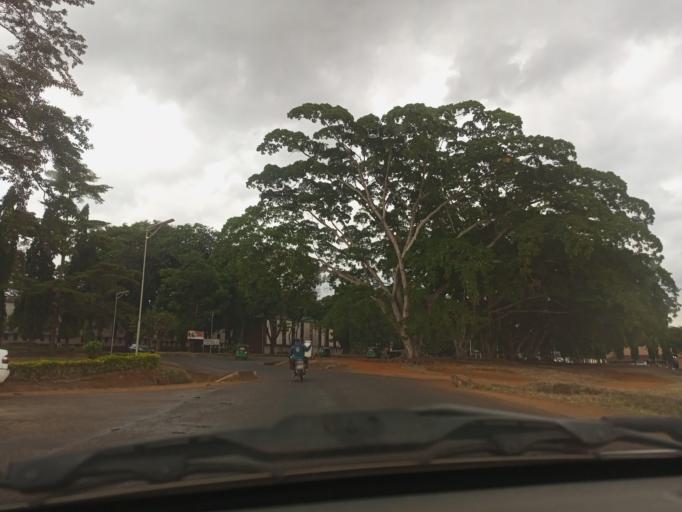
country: TZ
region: Morogoro
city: Morogoro
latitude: -6.8518
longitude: 37.6570
